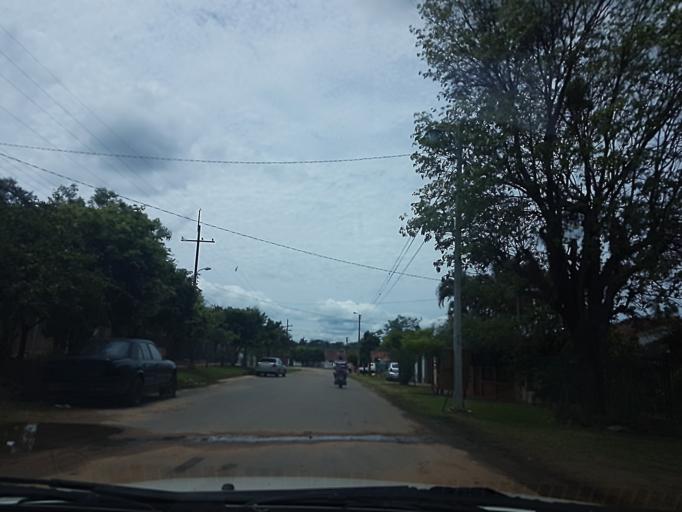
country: PY
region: Central
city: Colonia Mariano Roque Alonso
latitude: -25.1871
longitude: -57.5235
